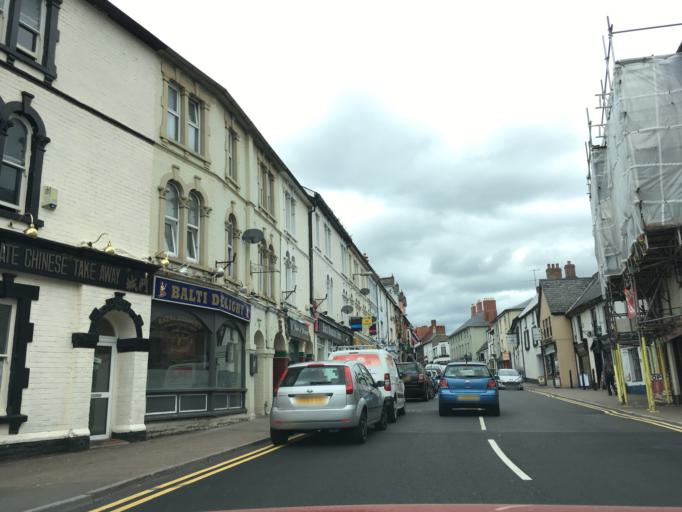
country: GB
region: Wales
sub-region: Monmouthshire
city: Abergavenny
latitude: 51.8201
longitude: -3.0162
